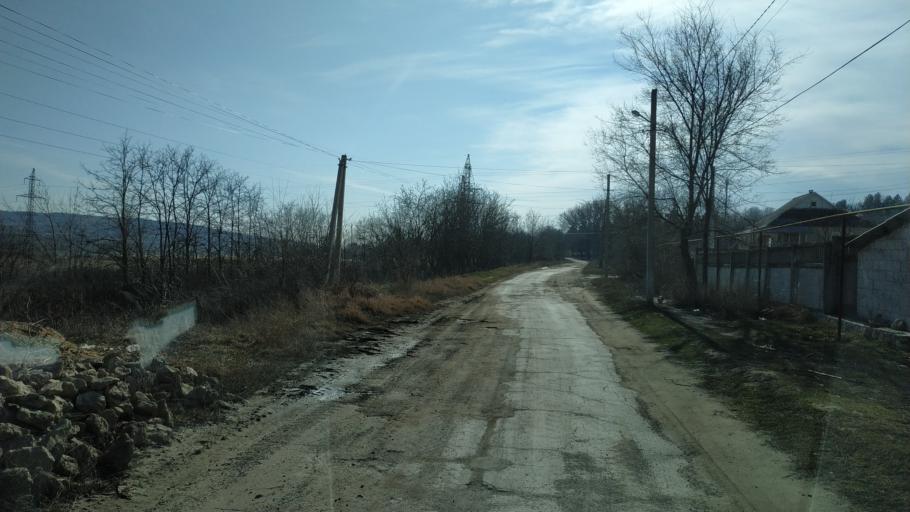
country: MD
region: Nisporeni
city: Nisporeni
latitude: 47.0621
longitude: 28.1716
